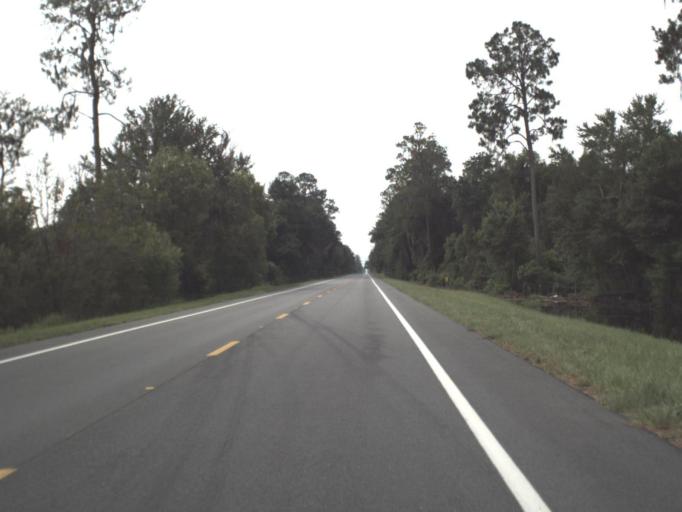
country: US
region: Florida
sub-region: Hamilton County
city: Jasper
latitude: 30.5342
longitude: -82.6769
